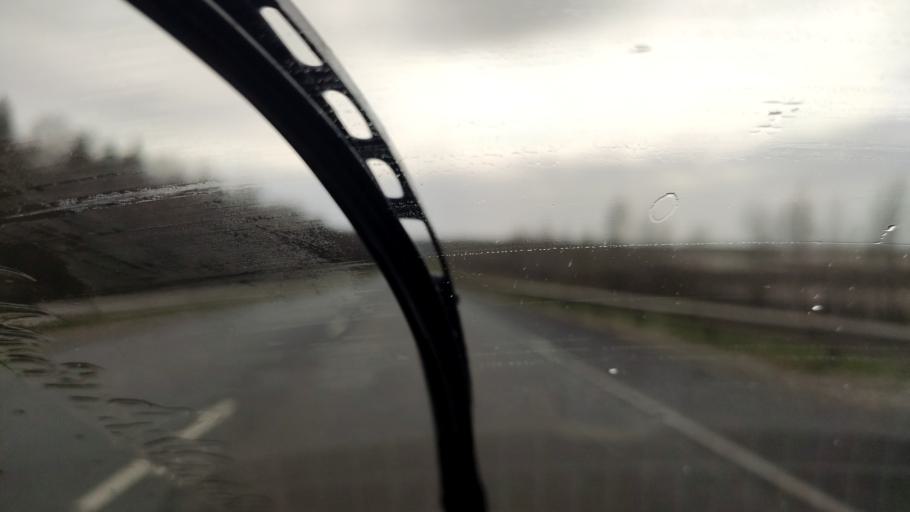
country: RU
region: Kursk
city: Gorshechnoye
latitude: 51.4770
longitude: 37.9503
